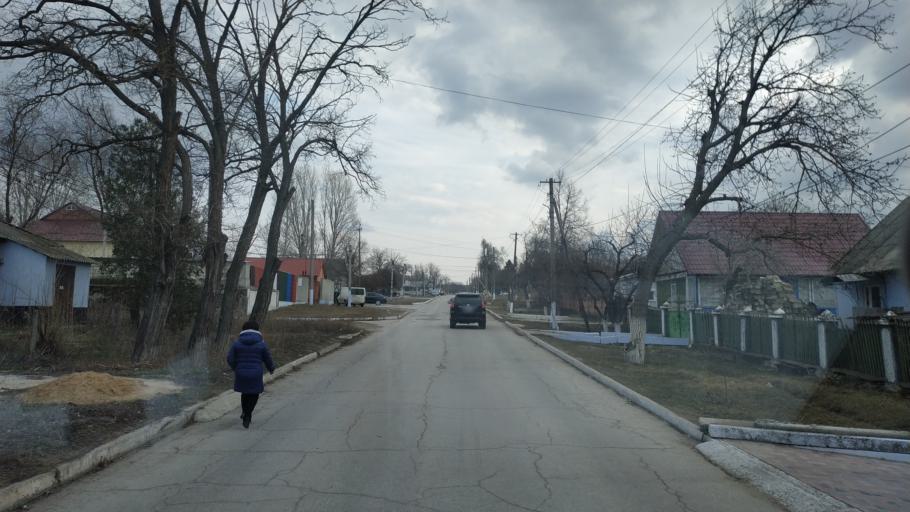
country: MD
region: Anenii Noi
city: Anenii Noi
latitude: 46.8868
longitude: 29.3102
